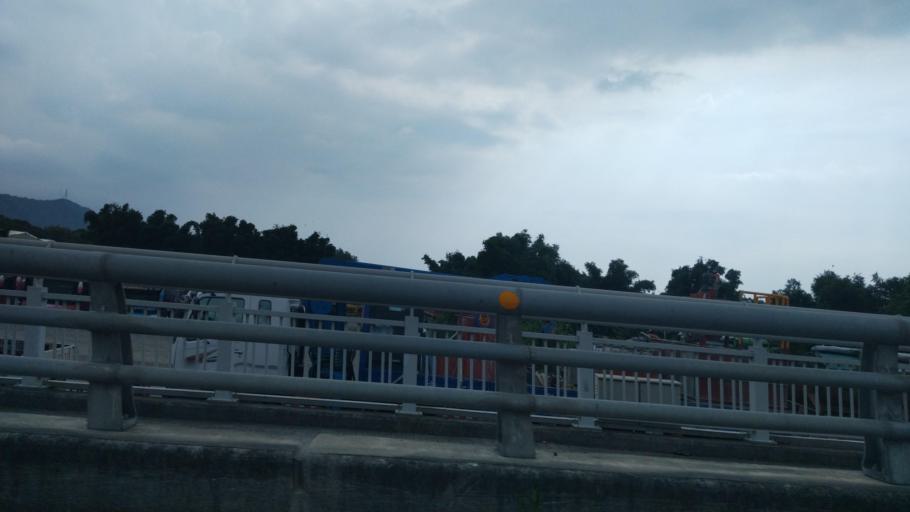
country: TW
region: Taiwan
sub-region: Taoyuan
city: Taoyuan
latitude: 24.9545
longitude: 121.3739
